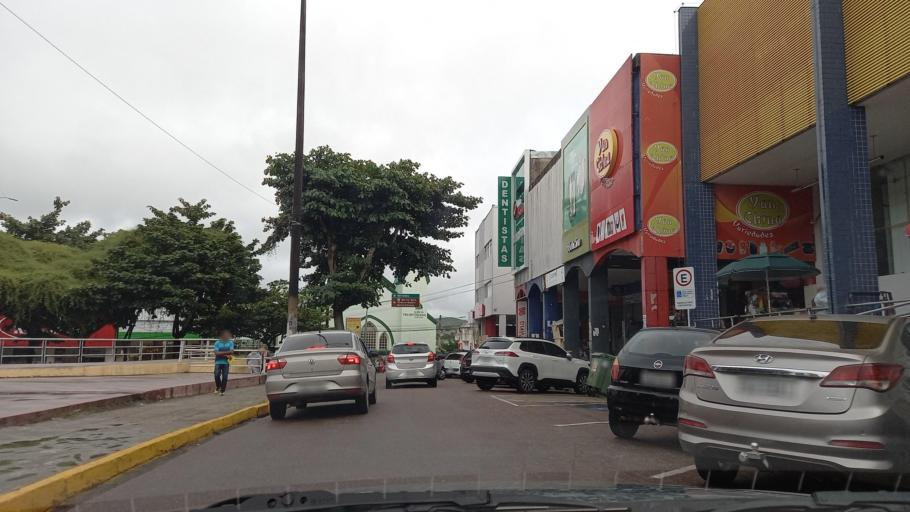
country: BR
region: Pernambuco
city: Garanhuns
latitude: -8.8910
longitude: -36.4959
